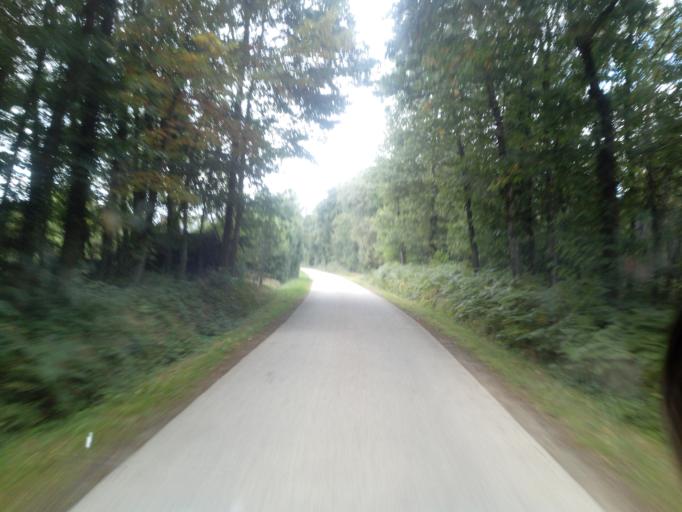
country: FR
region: Brittany
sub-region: Departement du Morbihan
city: Meneac
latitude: 48.1228
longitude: -2.4291
